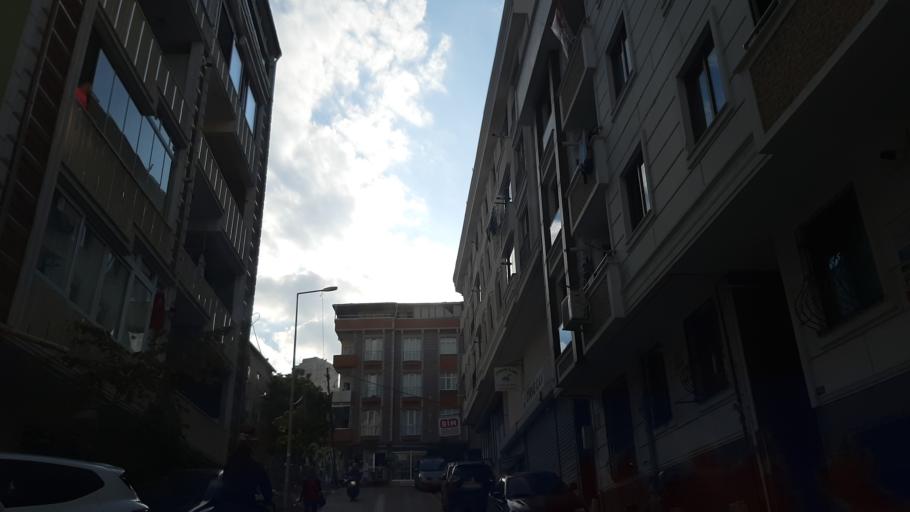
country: TR
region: Istanbul
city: Esenyurt
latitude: 41.0352
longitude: 28.6555
